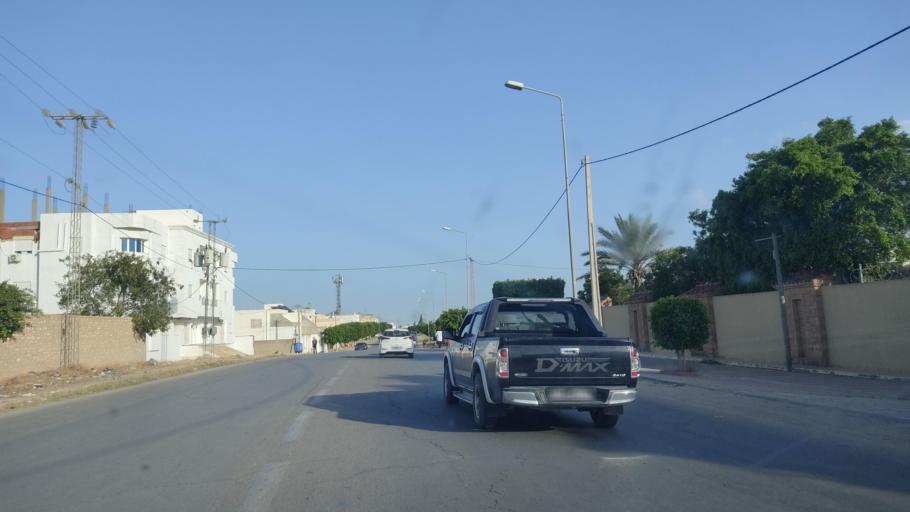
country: TN
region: Safaqis
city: Sfax
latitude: 34.7908
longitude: 10.6872
